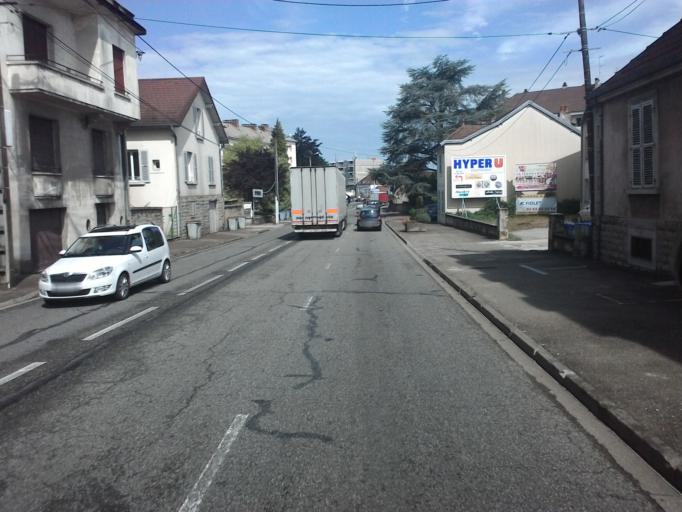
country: FR
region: Franche-Comte
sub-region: Departement du Jura
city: Lons-le-Saunier
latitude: 46.6713
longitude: 5.5445
